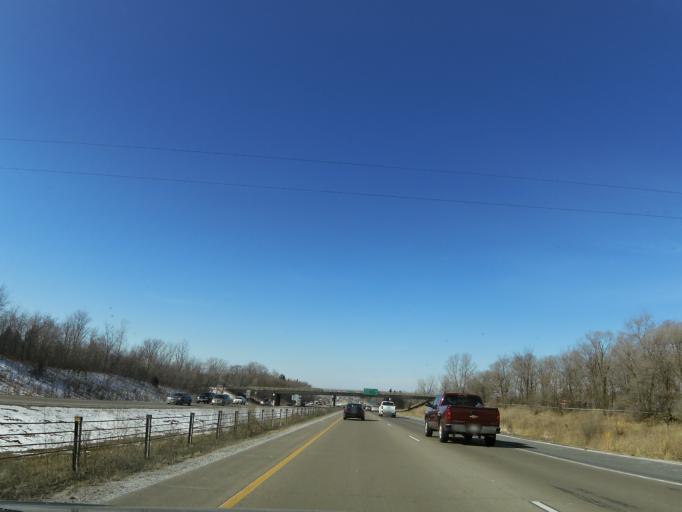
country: US
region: Minnesota
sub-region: Ramsey County
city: North Saint Paul
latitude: 45.0364
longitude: -93.0020
